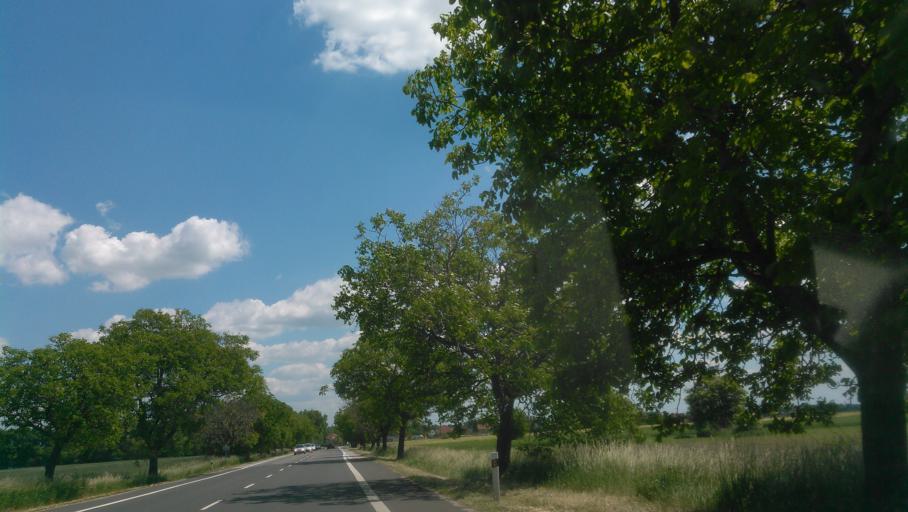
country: SK
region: Trnavsky
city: Dunajska Streda
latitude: 47.9711
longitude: 17.6735
